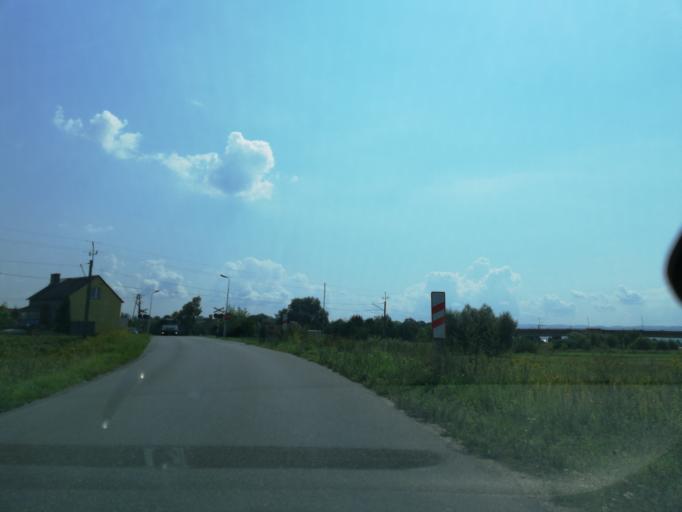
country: PL
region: Lesser Poland Voivodeship
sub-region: Powiat nowosadecki
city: Chelmiec
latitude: 49.6444
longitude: 20.6727
